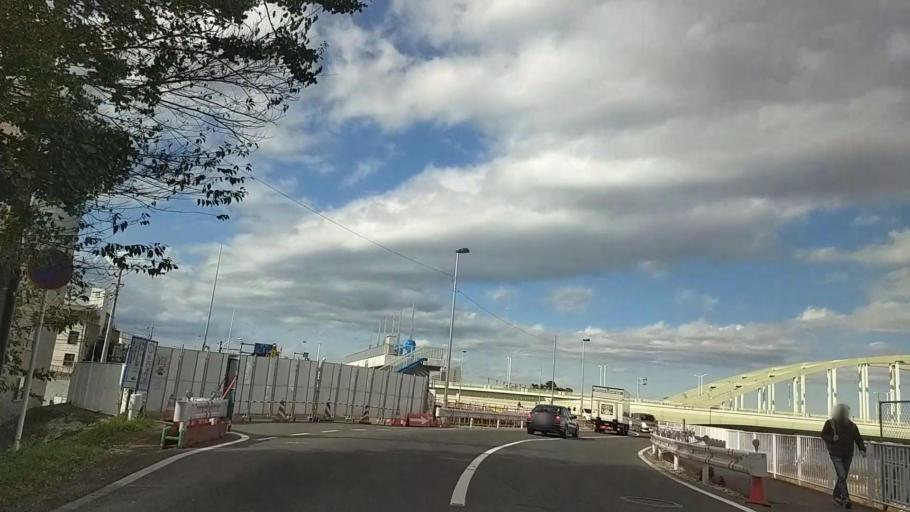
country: JP
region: Tokyo
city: Chofugaoka
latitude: 35.6228
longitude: 139.5690
